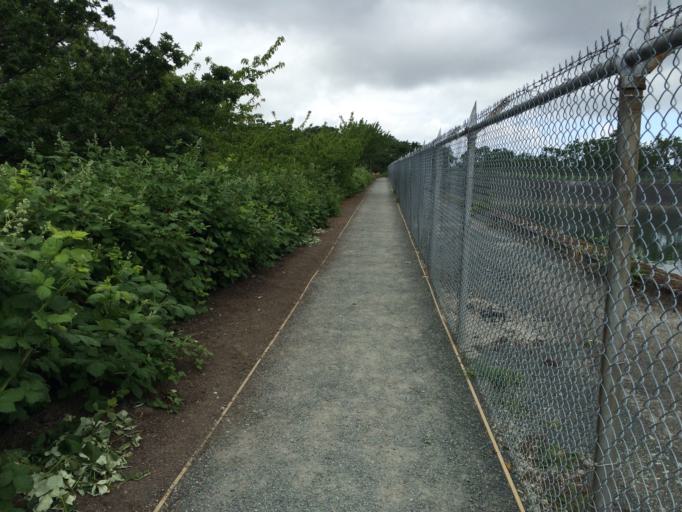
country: CA
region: British Columbia
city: Victoria
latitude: 48.4442
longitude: -123.3526
